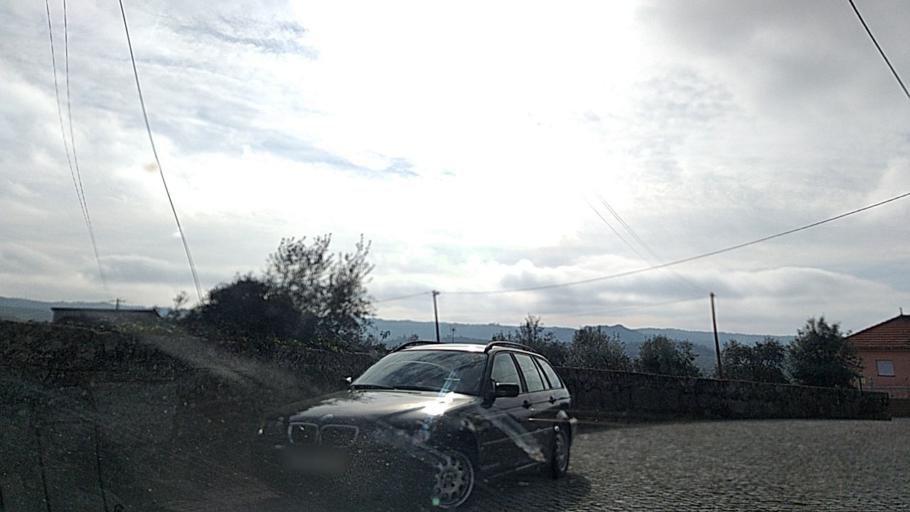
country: PT
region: Guarda
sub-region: Aguiar da Beira
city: Aguiar da Beira
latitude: 40.7313
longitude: -7.5564
